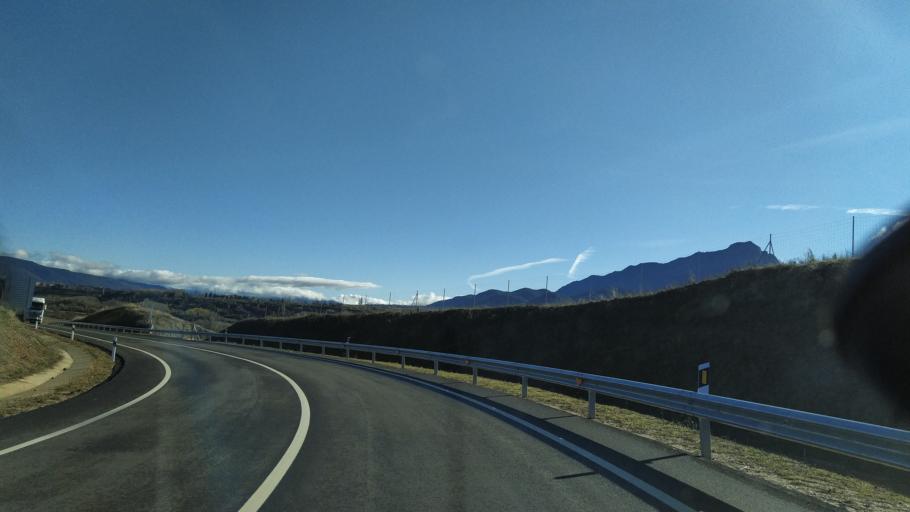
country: ES
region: Aragon
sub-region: Provincia de Huesca
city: Jaca
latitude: 42.5635
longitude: -0.6004
